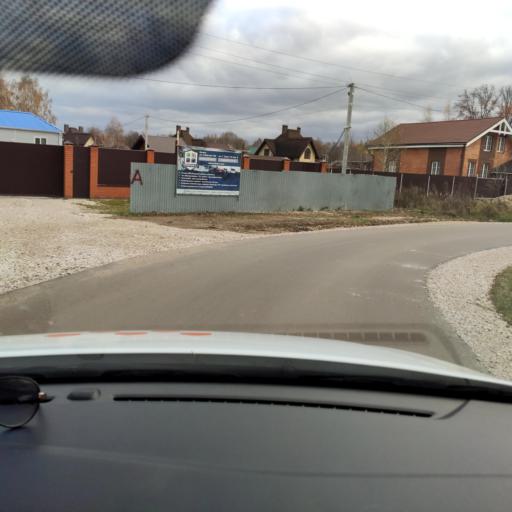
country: RU
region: Tatarstan
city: Stolbishchi
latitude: 55.7366
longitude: 49.2681
